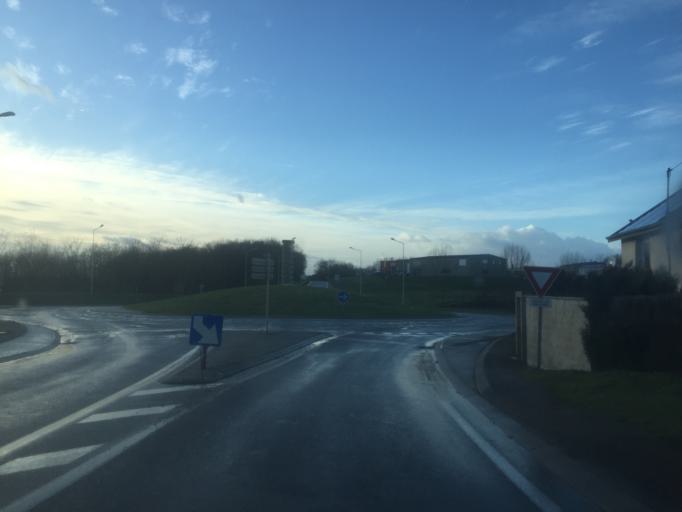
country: FR
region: Franche-Comte
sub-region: Departement du Jura
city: Dampierre
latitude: 47.1512
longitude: 5.7194
